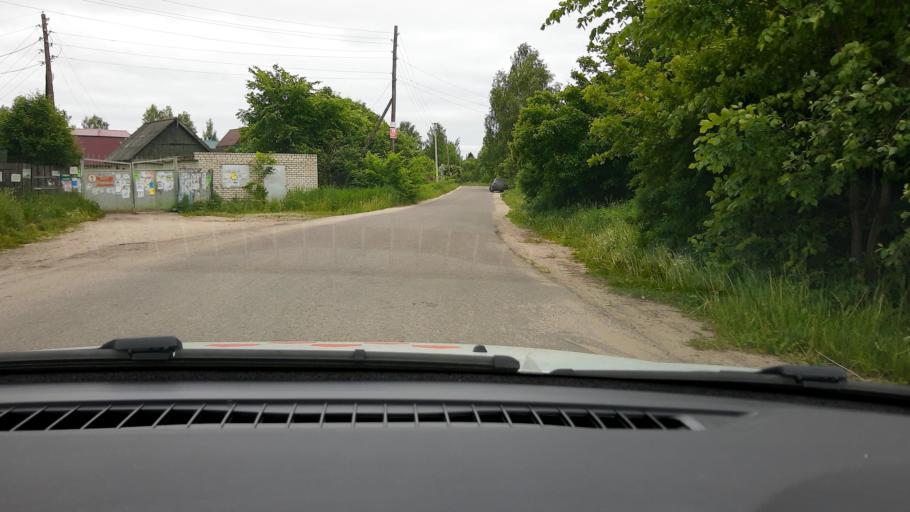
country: RU
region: Nizjnij Novgorod
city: Sitniki
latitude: 56.5197
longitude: 44.0501
